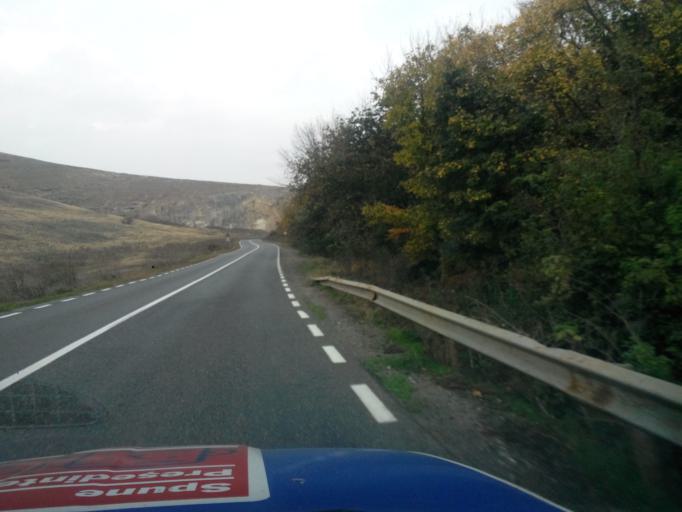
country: RO
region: Tulcea
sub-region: Comuna Somova
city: Somova
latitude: 45.1814
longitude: 28.6192
